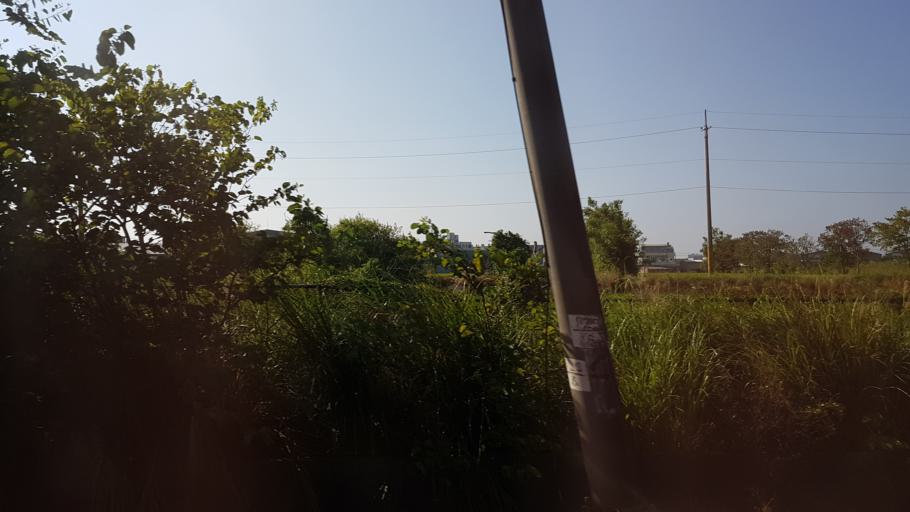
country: TW
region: Taiwan
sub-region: Miaoli
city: Miaoli
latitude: 24.6562
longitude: 120.8765
